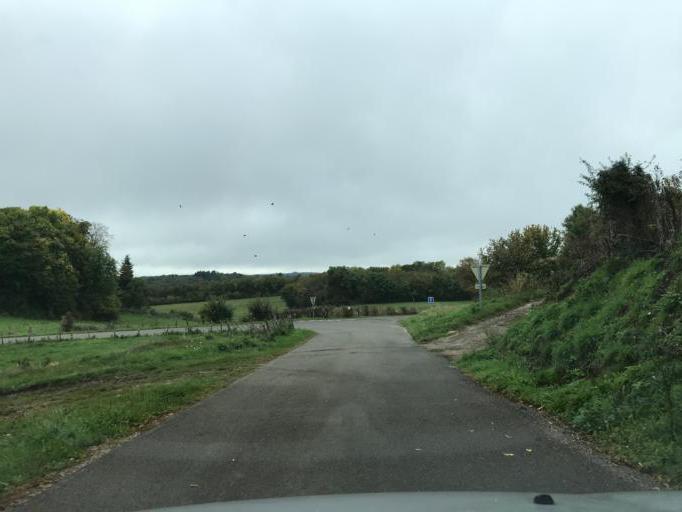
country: FR
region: Franche-Comte
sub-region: Departement du Jura
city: Arinthod
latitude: 46.4533
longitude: 5.5103
